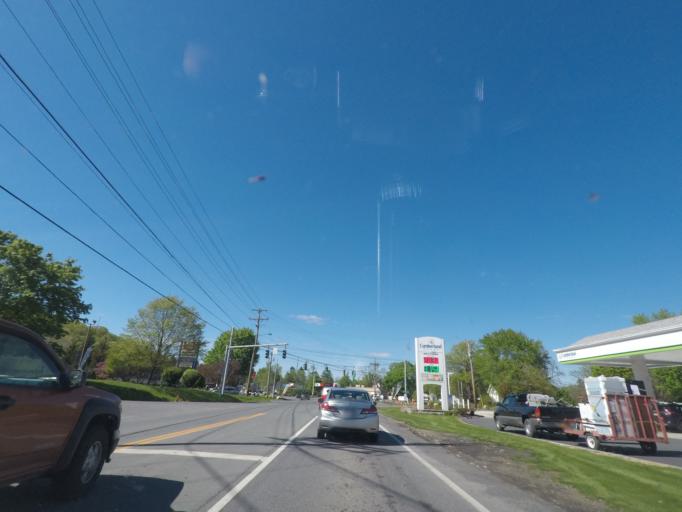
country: US
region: New York
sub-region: Albany County
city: Ravena
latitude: 42.4678
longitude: -73.8162
